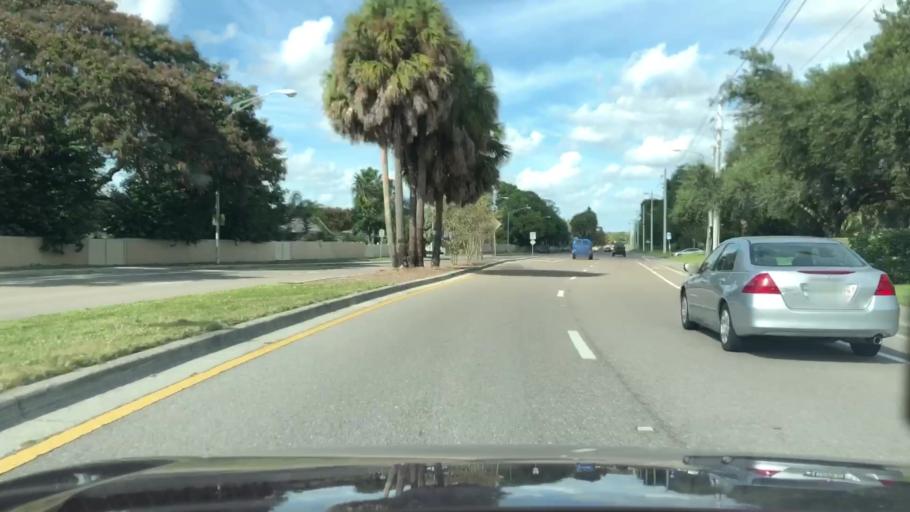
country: US
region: Florida
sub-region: Sarasota County
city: Sarasota Springs
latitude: 27.3175
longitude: -82.4828
